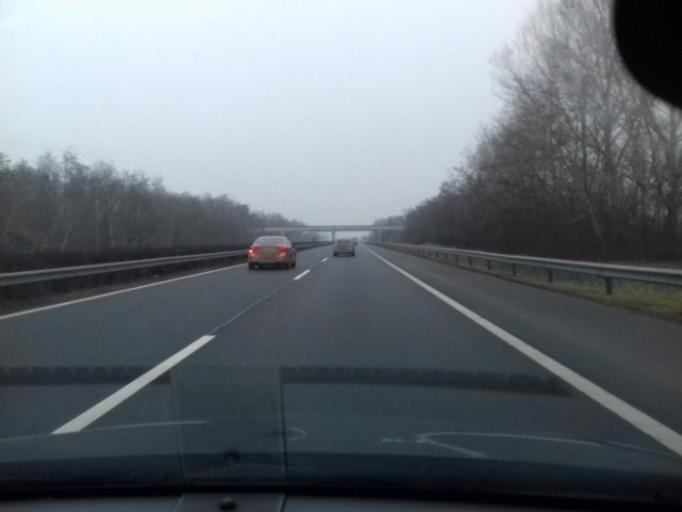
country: HU
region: Heves
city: Kal
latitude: 47.7224
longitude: 20.3017
